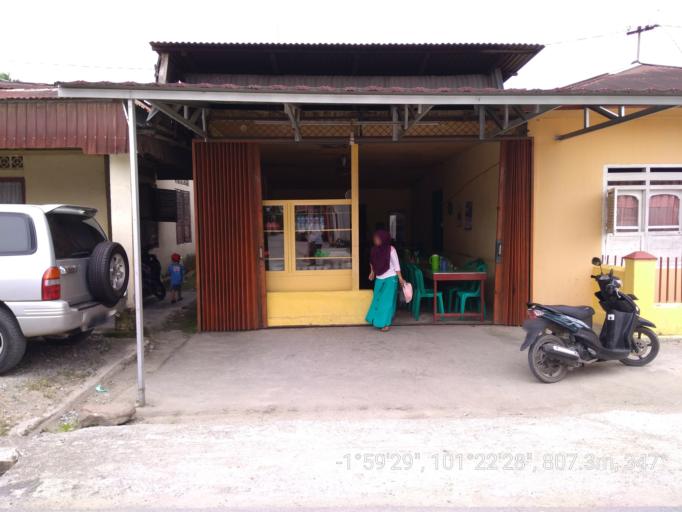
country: ID
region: Jambi
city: Semurup
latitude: -1.9916
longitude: 101.3746
